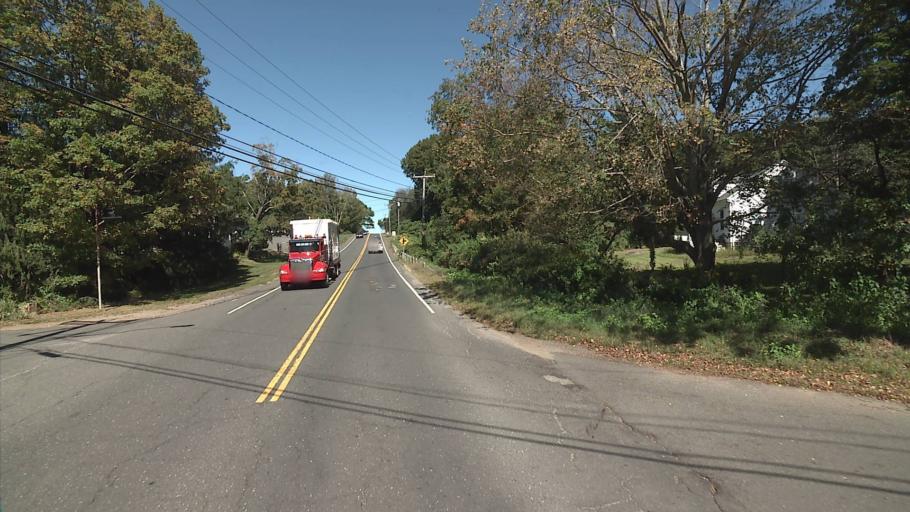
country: US
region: Connecticut
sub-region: New Haven County
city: Prospect
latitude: 41.4708
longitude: -72.9675
